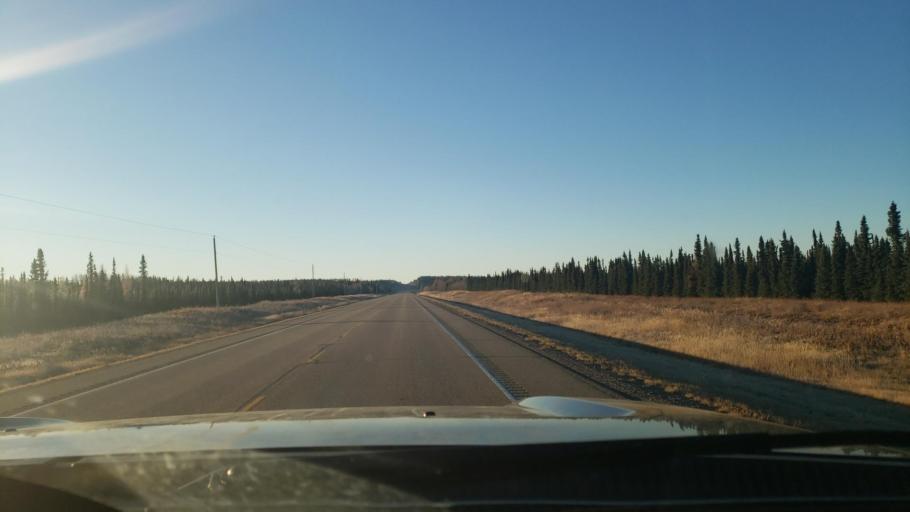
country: CA
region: British Columbia
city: Fort Nelson
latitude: 58.4513
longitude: -122.7152
